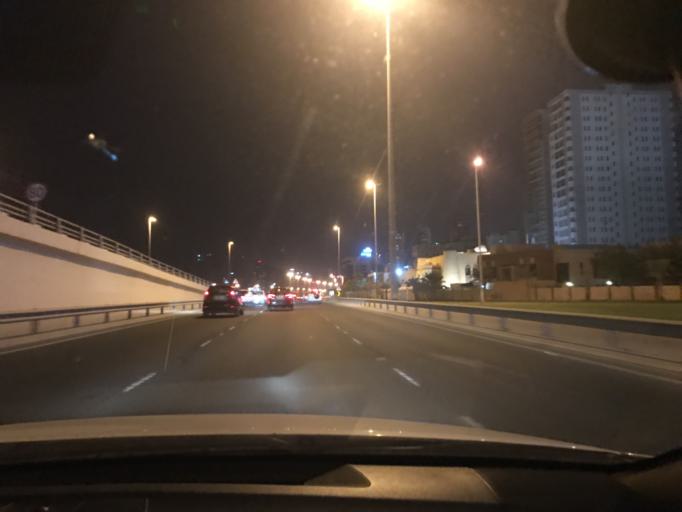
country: BH
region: Muharraq
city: Al Muharraq
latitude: 26.2413
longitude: 50.5942
